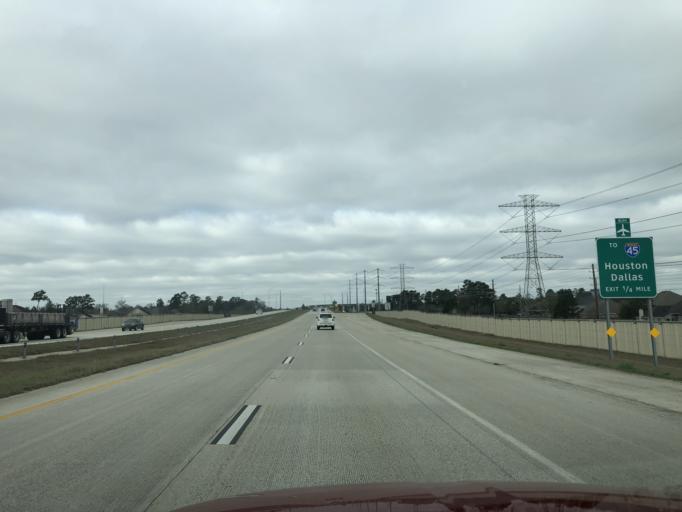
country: US
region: Texas
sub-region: Harris County
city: Spring
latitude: 30.0927
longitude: -95.4232
